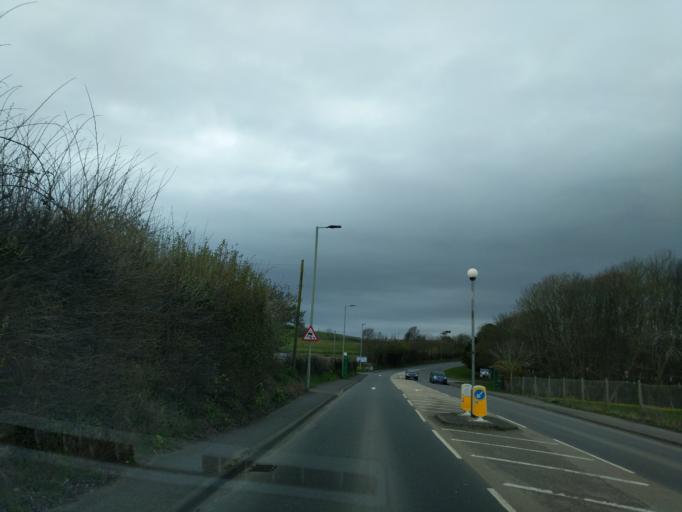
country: GB
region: England
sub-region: Devon
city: Appledore
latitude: 51.0430
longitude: -4.2052
